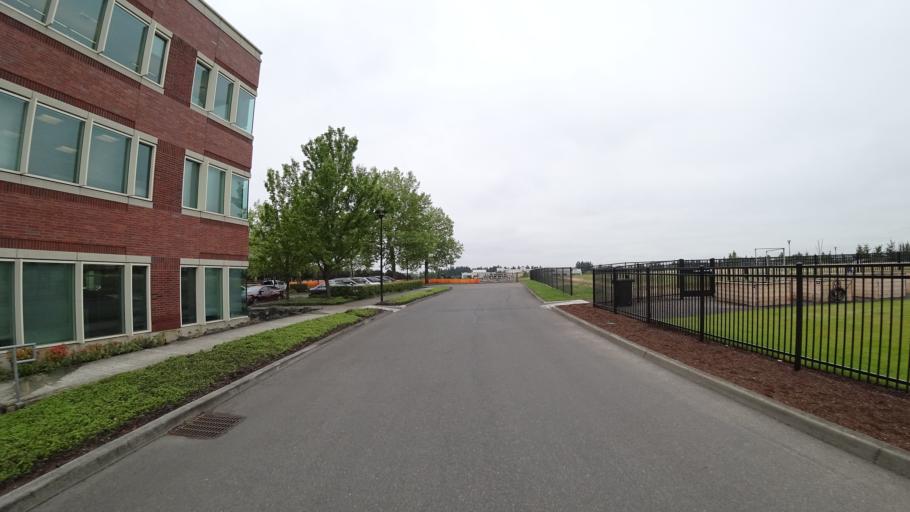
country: US
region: Oregon
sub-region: Washington County
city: Rockcreek
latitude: 45.5432
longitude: -122.8747
